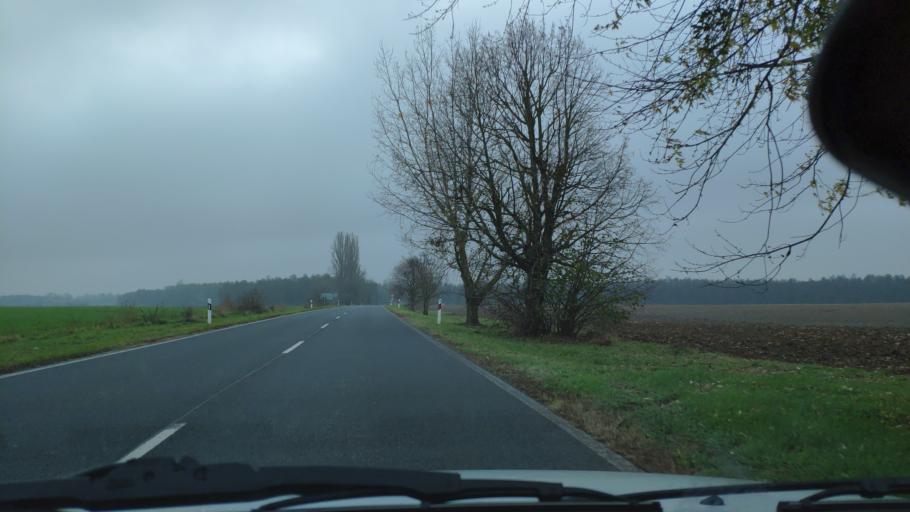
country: HU
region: Somogy
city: Balatonbereny
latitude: 46.6195
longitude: 17.2831
